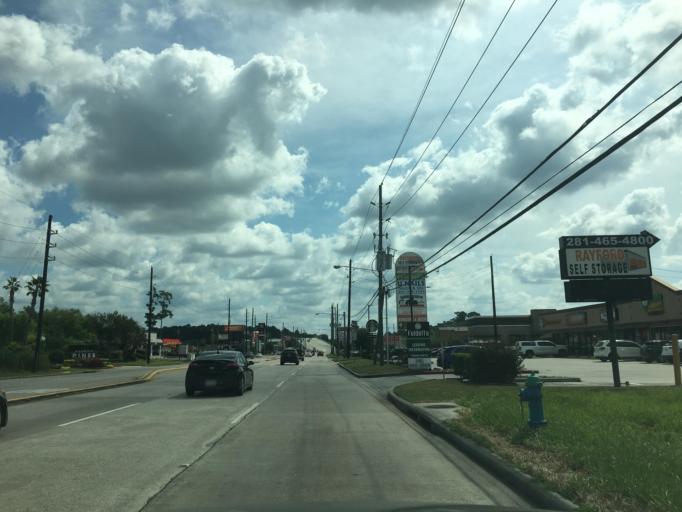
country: US
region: Texas
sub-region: Montgomery County
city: Oak Ridge North
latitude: 30.1271
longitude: -95.4359
